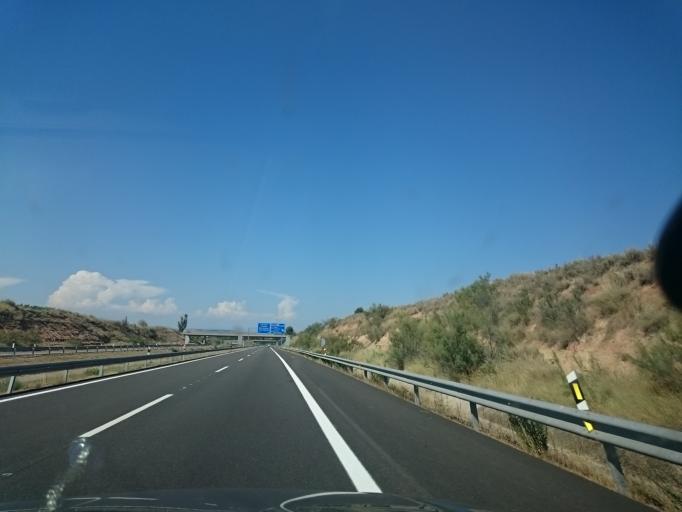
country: ES
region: Catalonia
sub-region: Provincia de Lleida
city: Soses
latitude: 41.5284
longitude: 0.4701
